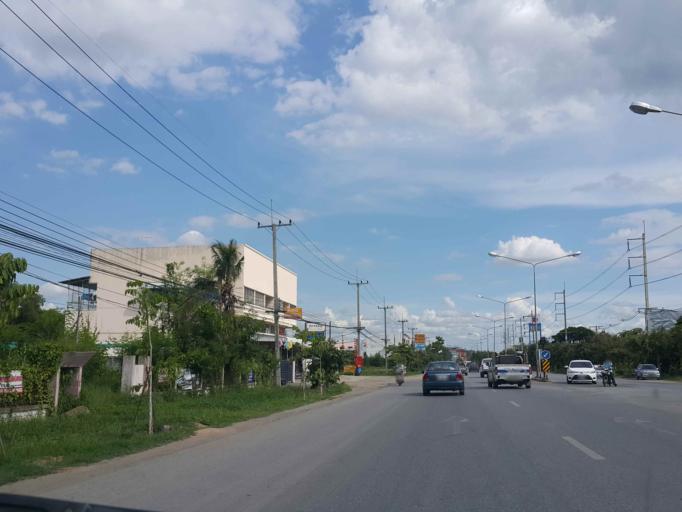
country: TH
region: Chiang Mai
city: San Sai
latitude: 18.8785
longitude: 99.0150
